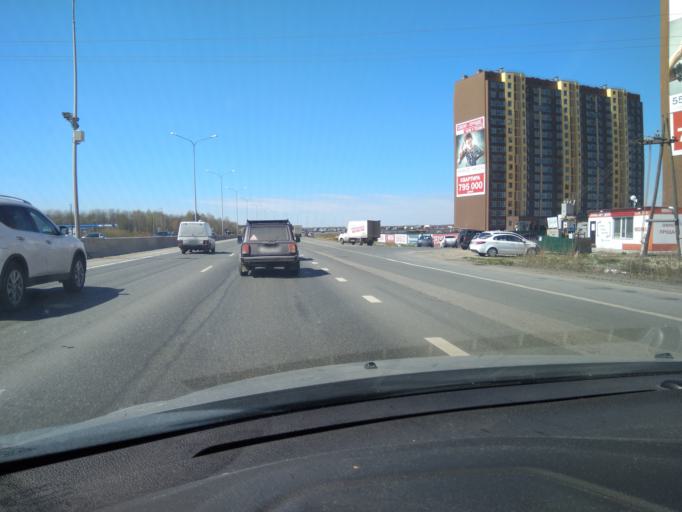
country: RU
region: Tjumen
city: Moskovskiy
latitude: 57.1333
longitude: 65.4680
